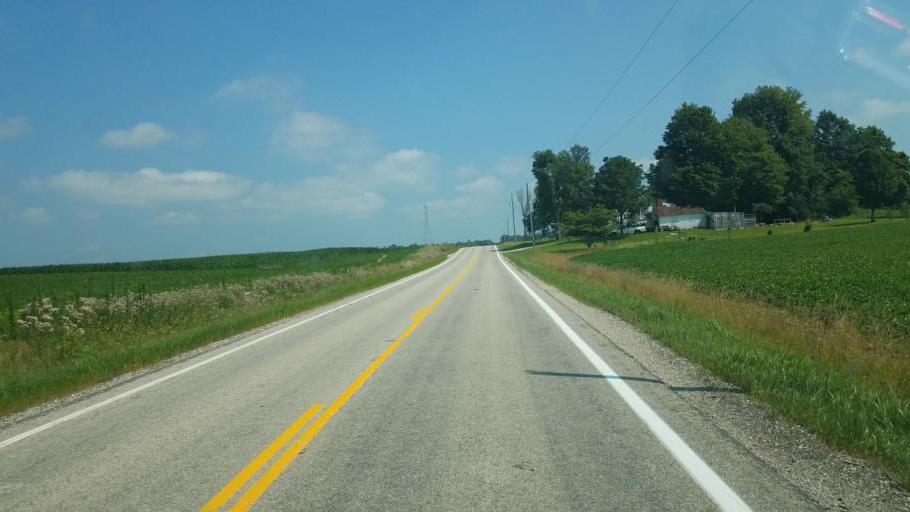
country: US
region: Ohio
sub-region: Crawford County
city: Bucyrus
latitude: 40.8494
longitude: -82.8556
